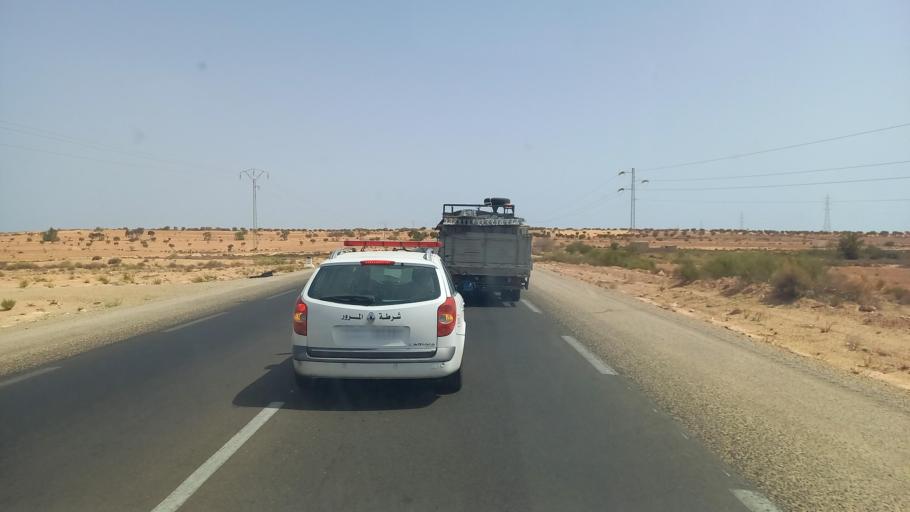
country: TN
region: Madanin
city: Zarzis
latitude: 33.4115
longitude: 10.8660
